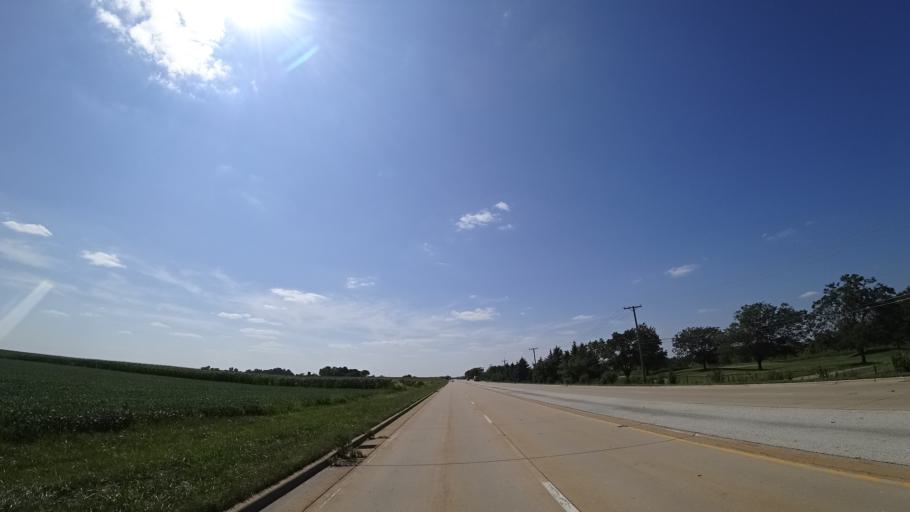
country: US
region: Illinois
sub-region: Will County
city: Frankfort Square
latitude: 41.5280
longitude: -87.7731
